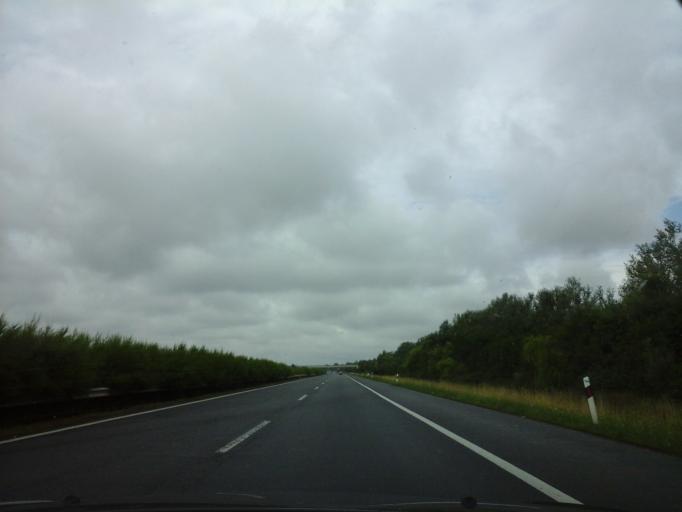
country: HU
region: Borsod-Abauj-Zemplen
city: Hejobaba
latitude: 47.8686
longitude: 20.9766
